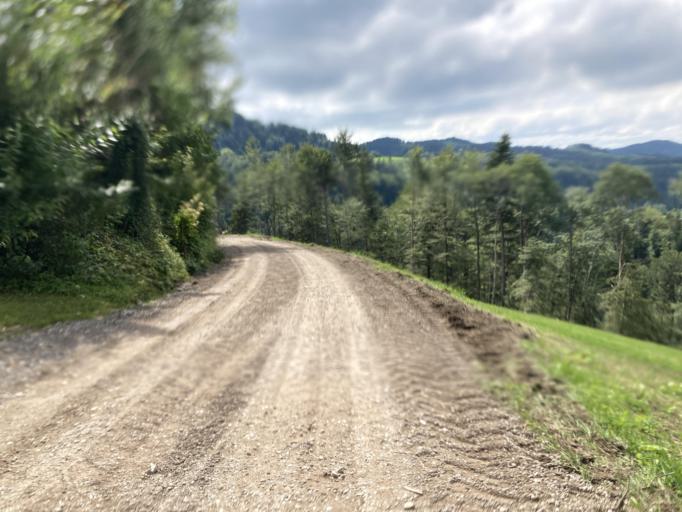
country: CH
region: Zurich
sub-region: Bezirk Pfaeffikon
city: Bauma
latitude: 47.3589
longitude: 8.9341
